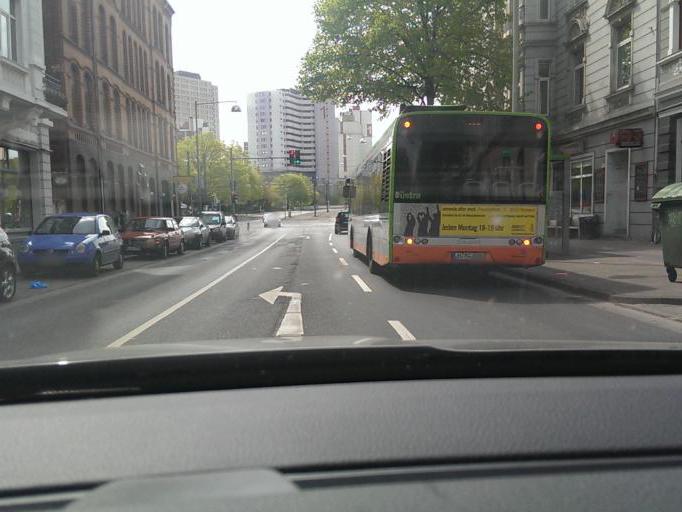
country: DE
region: Lower Saxony
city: Hannover
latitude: 52.3745
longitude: 9.7193
